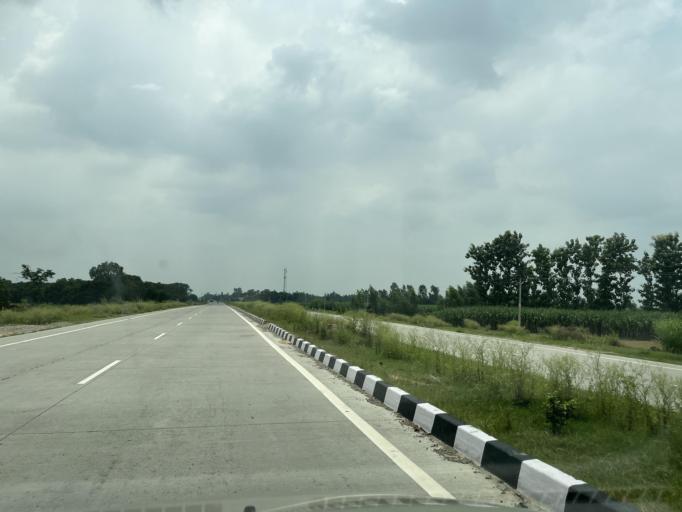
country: IN
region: Uttar Pradesh
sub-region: Bijnor
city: Najibabad
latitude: 29.5543
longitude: 78.3392
